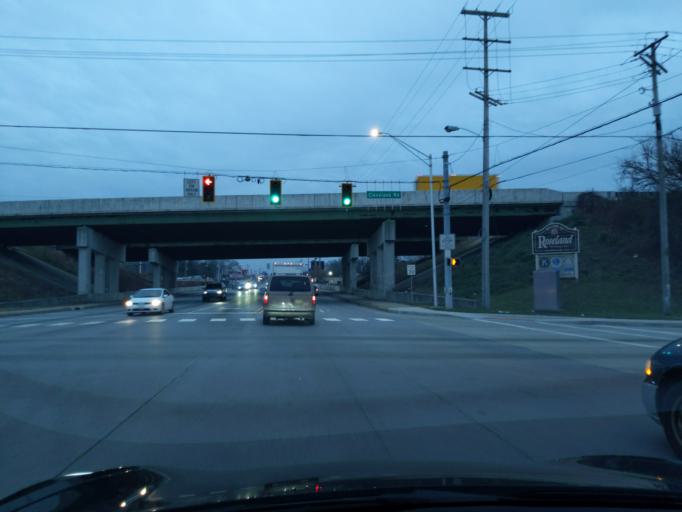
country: US
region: Indiana
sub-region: Saint Joseph County
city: Georgetown
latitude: 41.7205
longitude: -86.2502
